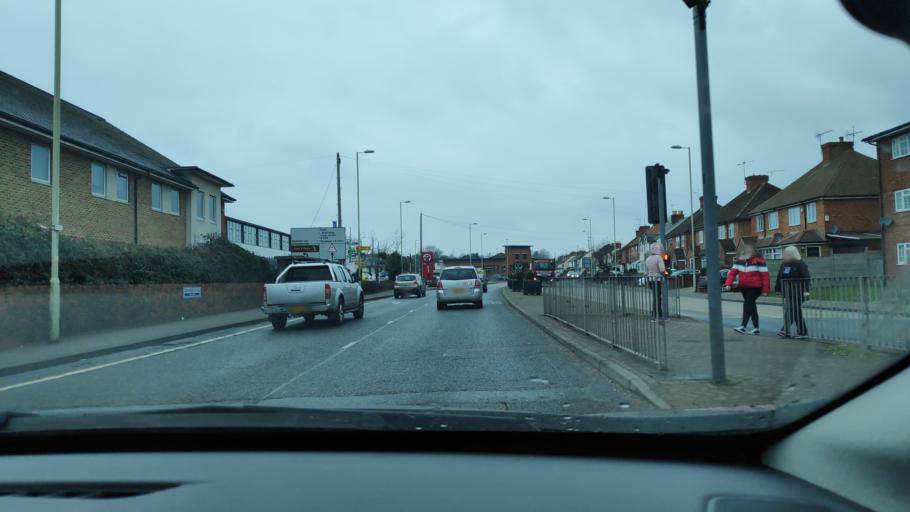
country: GB
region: England
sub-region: Hampshire
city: Aldershot
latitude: 51.2417
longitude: -0.7406
